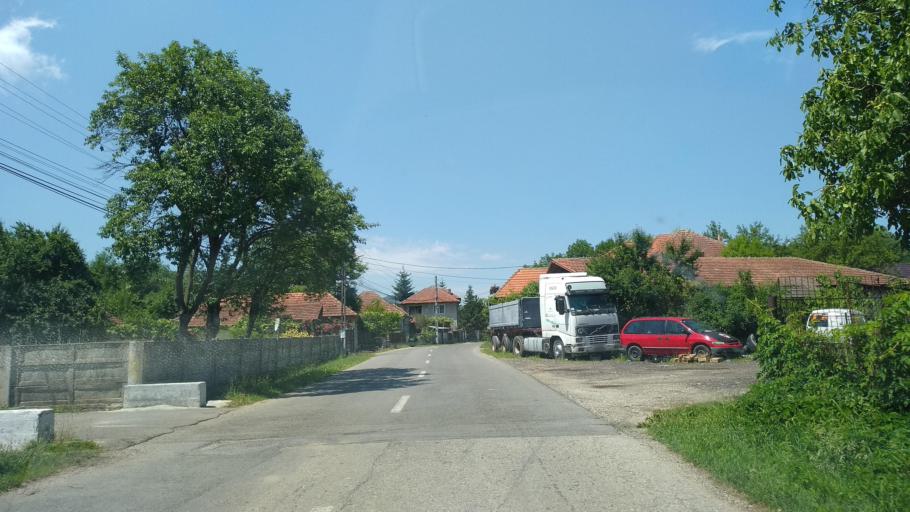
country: RO
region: Hunedoara
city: Densus
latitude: 45.5801
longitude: 22.8103
